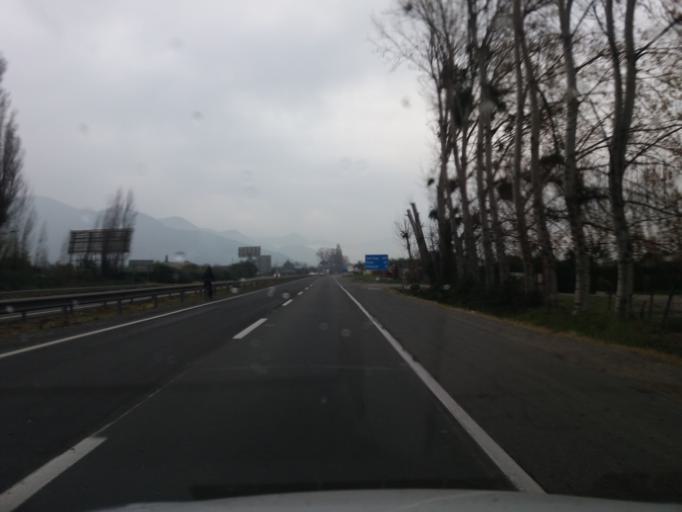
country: CL
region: Valparaiso
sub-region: Provincia de Quillota
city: Hacienda La Calera
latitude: -32.7903
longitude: -71.1657
